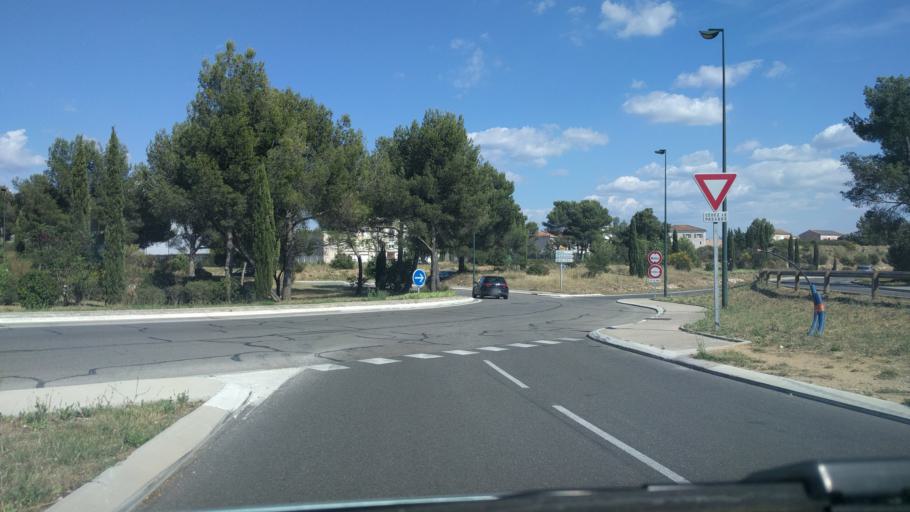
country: FR
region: Provence-Alpes-Cote d'Azur
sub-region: Departement des Bouches-du-Rhone
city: Cabries
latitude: 43.4953
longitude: 5.3496
